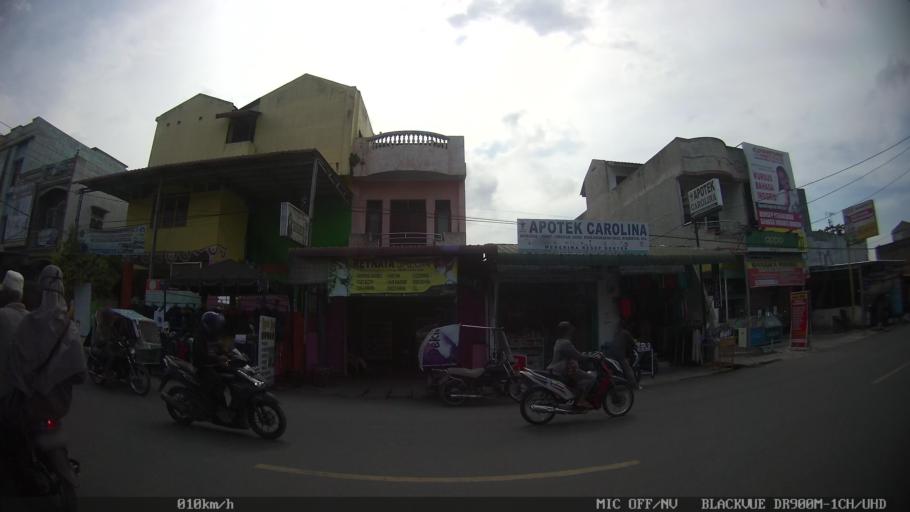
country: ID
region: North Sumatra
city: Medan
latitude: 3.6038
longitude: 98.7577
